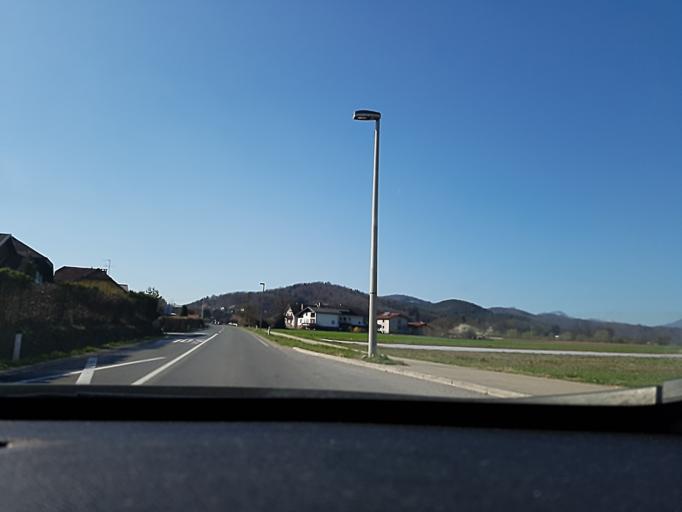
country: SI
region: Trzin
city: Trzin
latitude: 46.1005
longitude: 14.5534
